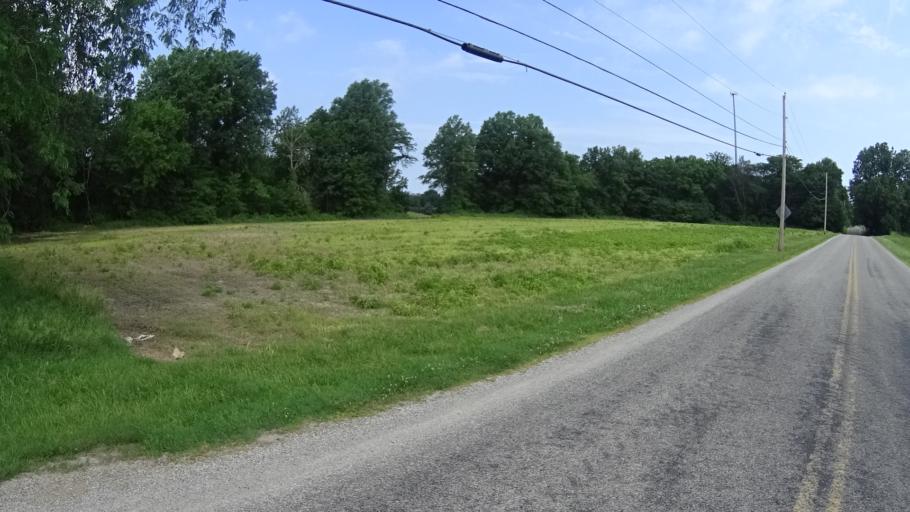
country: US
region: Ohio
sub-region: Lorain County
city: Vermilion
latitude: 41.3828
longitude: -82.4302
